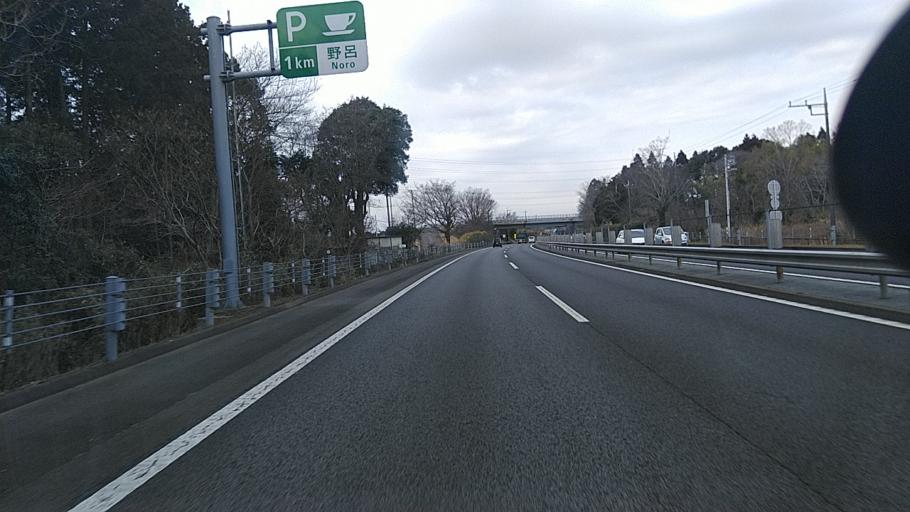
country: JP
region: Chiba
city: Oami
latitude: 35.5689
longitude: 140.2479
